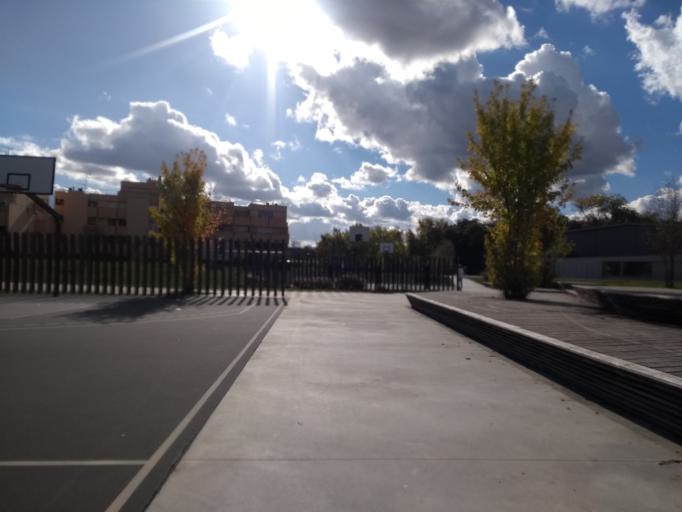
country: FR
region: Aquitaine
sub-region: Departement de la Gironde
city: Gradignan
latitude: 44.7730
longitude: -0.5974
